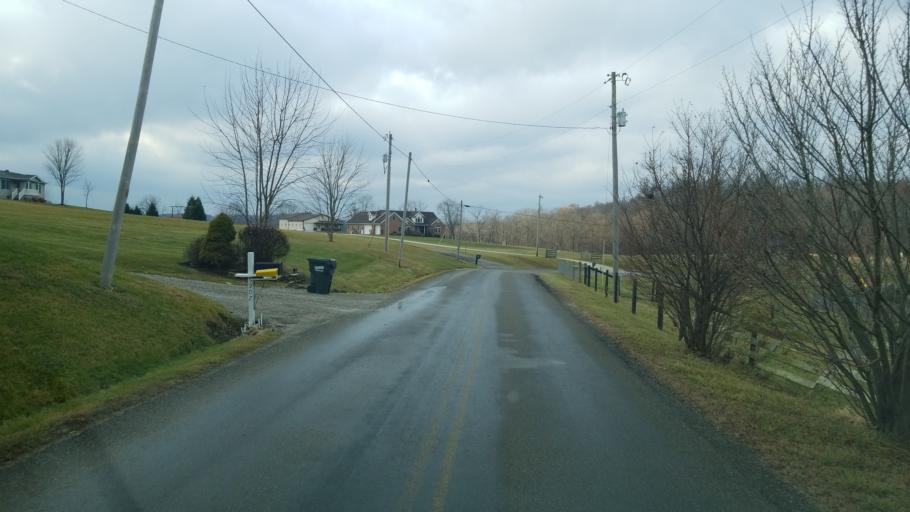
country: US
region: Ohio
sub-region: Holmes County
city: Millersburg
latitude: 40.5767
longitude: -81.9629
